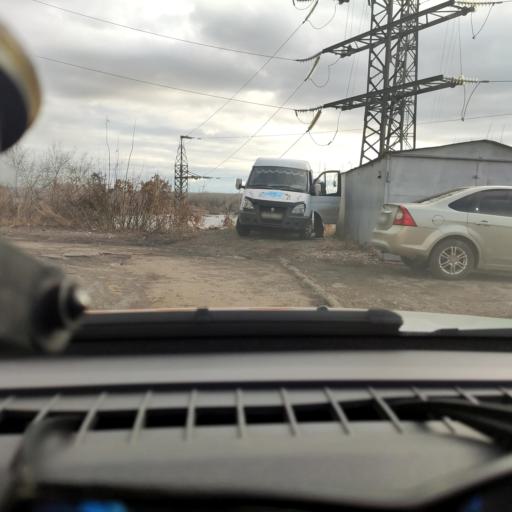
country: RU
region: Samara
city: Samara
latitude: 53.1709
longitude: 50.1897
